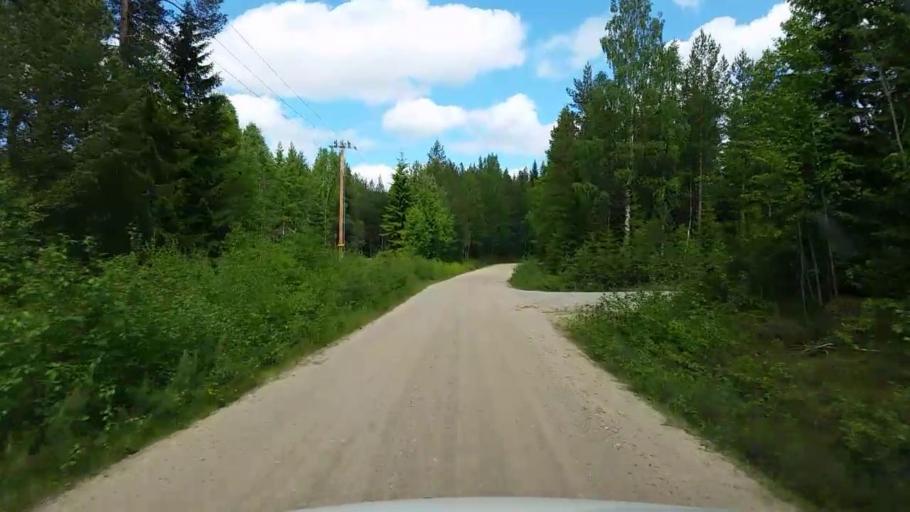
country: SE
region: Gaevleborg
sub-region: Ovanakers Kommun
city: Alfta
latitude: 61.5559
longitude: 15.9732
